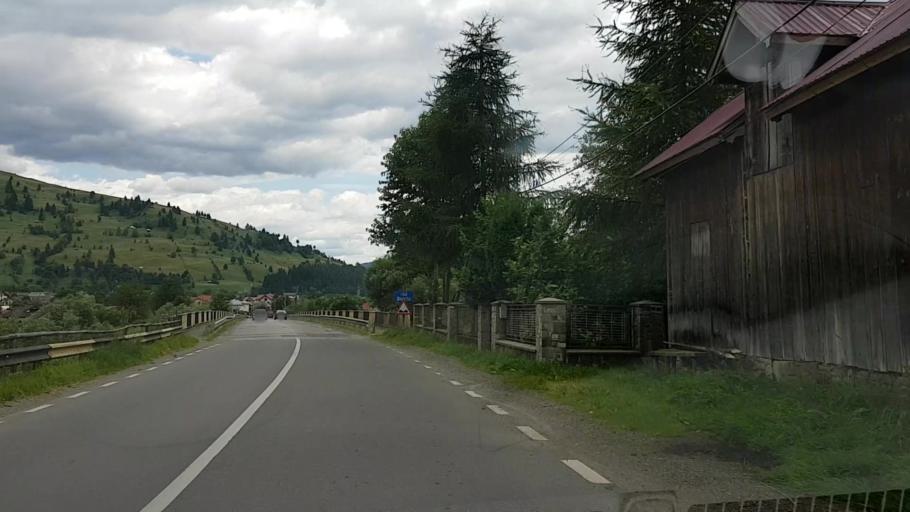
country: RO
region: Neamt
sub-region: Comuna Borca
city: Borca
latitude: 47.1843
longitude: 25.7755
